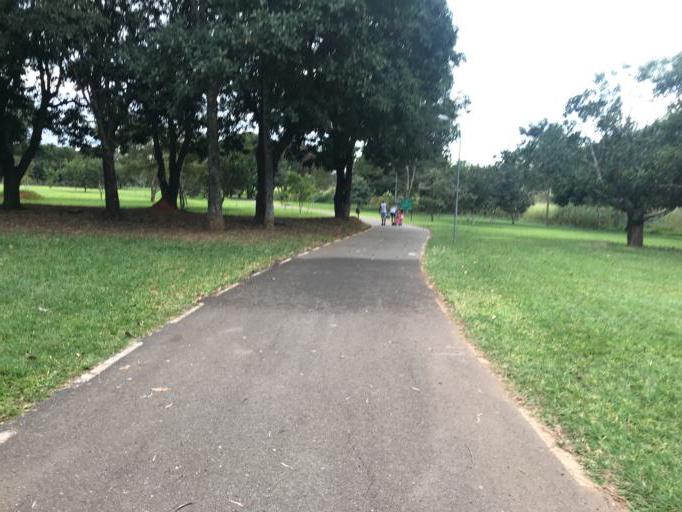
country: BR
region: Federal District
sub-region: Brasilia
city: Brasilia
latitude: -15.8346
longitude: -48.0230
